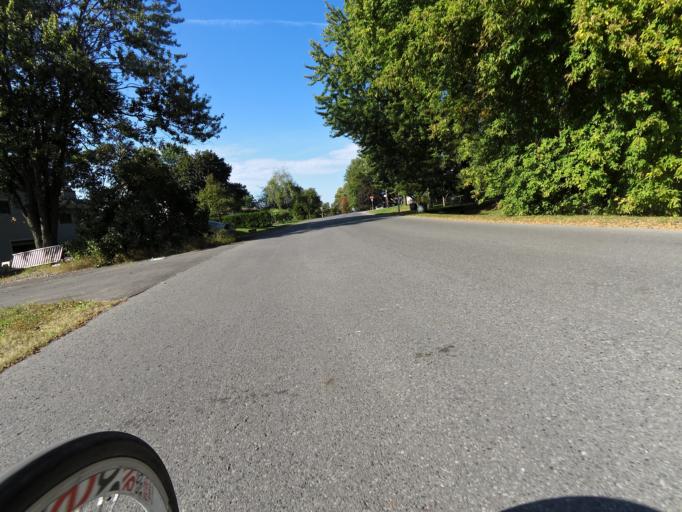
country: CA
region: Ontario
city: Bells Corners
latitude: 45.2384
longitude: -75.6985
